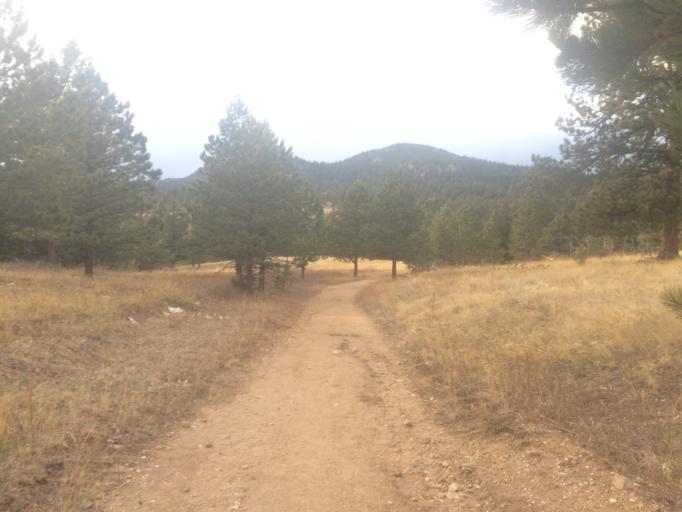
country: US
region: Colorado
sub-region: Boulder County
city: Coal Creek
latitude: 39.9607
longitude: -105.3441
